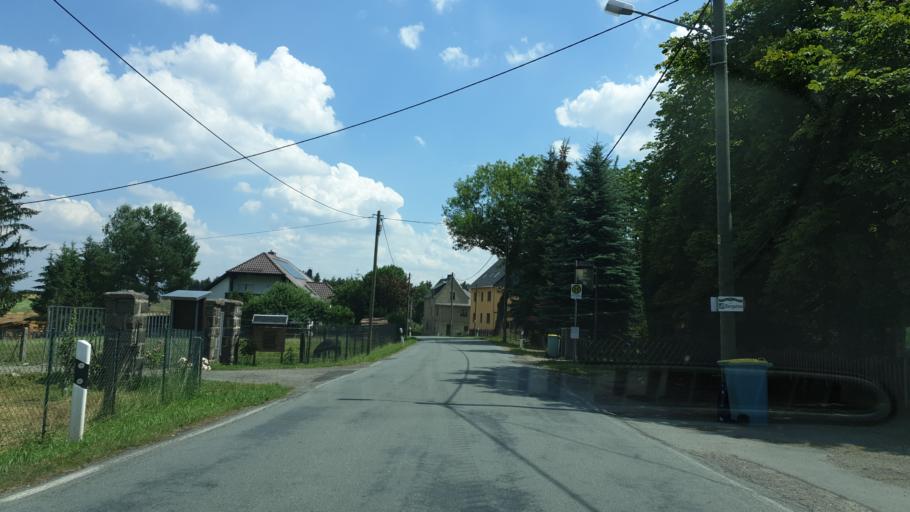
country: DE
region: Saxony
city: Kirchberg
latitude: 50.8021
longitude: 12.7737
